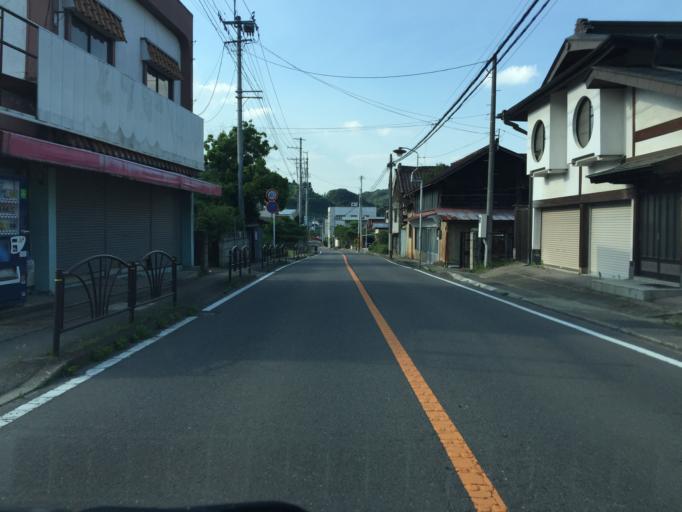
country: JP
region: Fukushima
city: Nihommatsu
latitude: 37.5589
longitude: 140.4129
